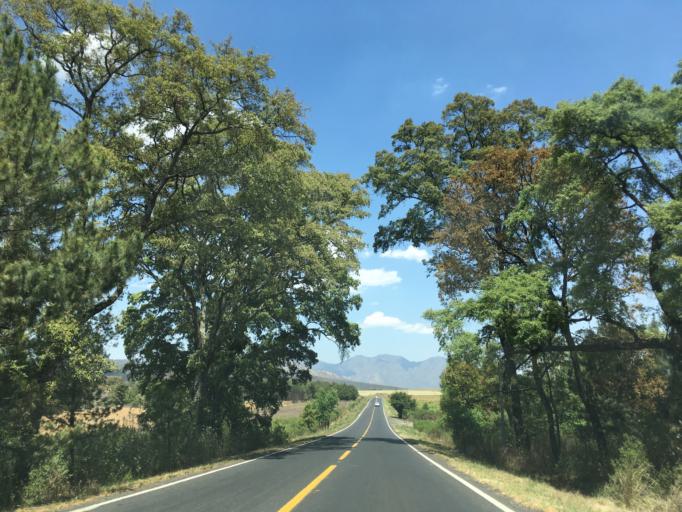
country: MX
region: Mexico
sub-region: Chalco
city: Zopoco
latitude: 19.7862
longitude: -102.0228
